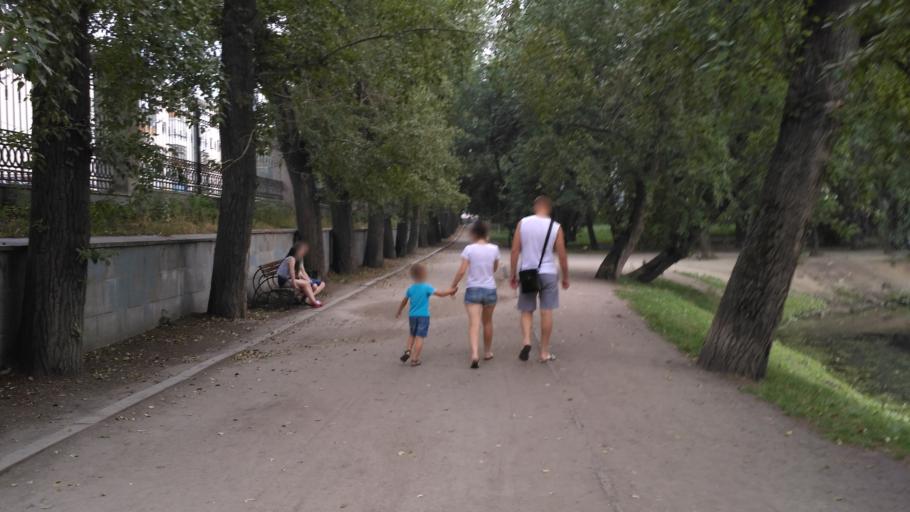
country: RU
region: Sverdlovsk
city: Yekaterinburg
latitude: 56.8467
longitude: 60.6151
